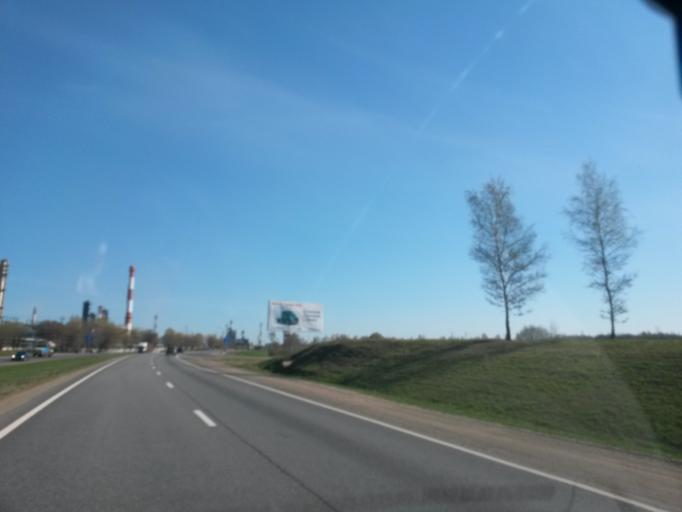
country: RU
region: Jaroslavl
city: Krasnyye Tkachi
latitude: 57.5320
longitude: 39.7854
